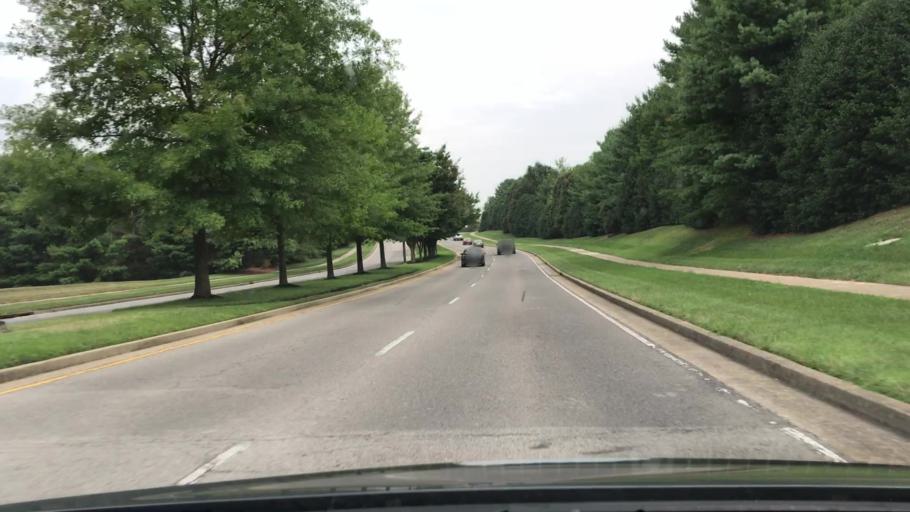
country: US
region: Tennessee
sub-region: Williamson County
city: Franklin
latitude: 35.9407
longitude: -86.7979
